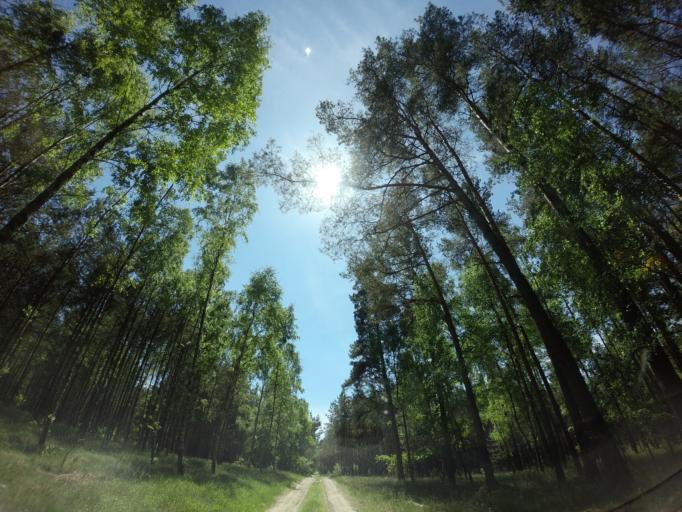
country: PL
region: West Pomeranian Voivodeship
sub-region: Powiat choszczenski
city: Drawno
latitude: 53.2499
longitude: 15.7523
